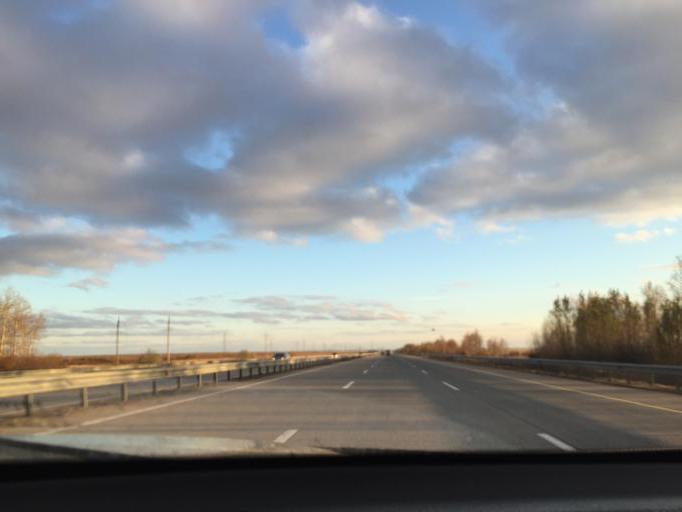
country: KZ
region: Astana Qalasy
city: Astana
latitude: 51.3281
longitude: 71.3450
